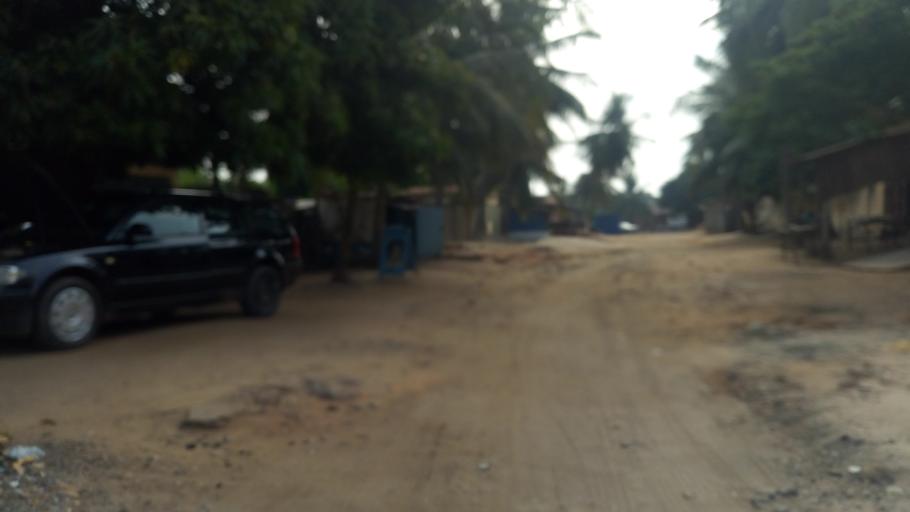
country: TG
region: Maritime
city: Lome
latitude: 6.1780
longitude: 1.1723
